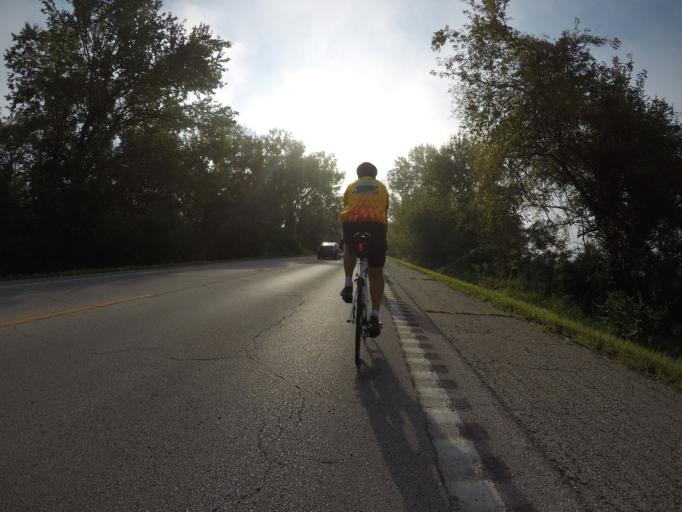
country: US
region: Kansas
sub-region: Leavenworth County
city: Leavenworth
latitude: 39.3291
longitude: -94.8852
